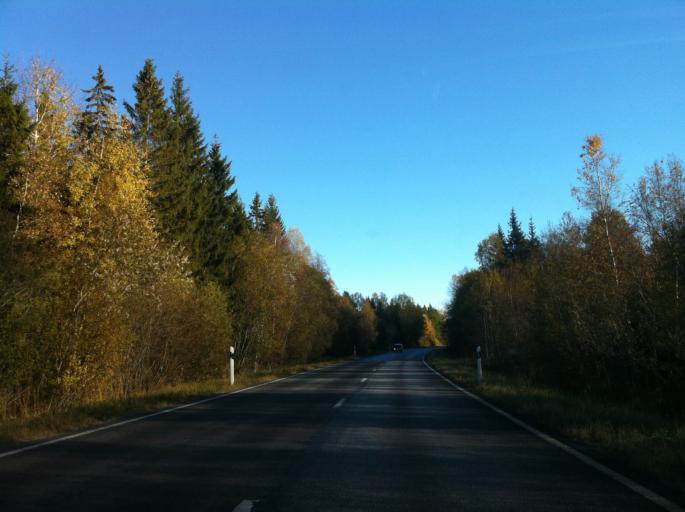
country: SE
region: Uppsala
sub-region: Osthammars Kommun
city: Oregrund
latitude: 60.3308
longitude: 18.3870
